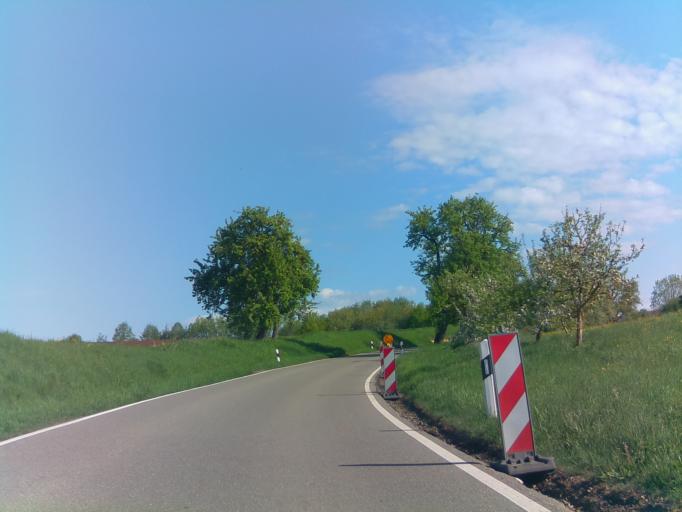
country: DE
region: Baden-Wuerttemberg
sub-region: Regierungsbezirk Stuttgart
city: Motzingen
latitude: 48.4997
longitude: 8.7741
